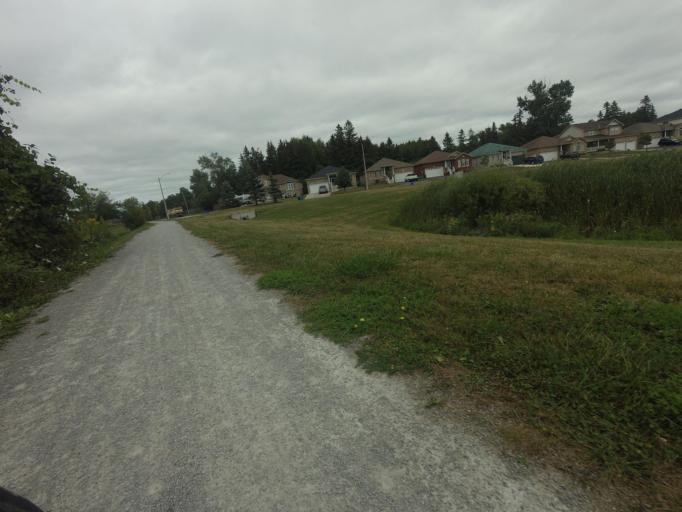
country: CA
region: Ontario
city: Omemee
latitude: 44.3377
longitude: -78.7487
